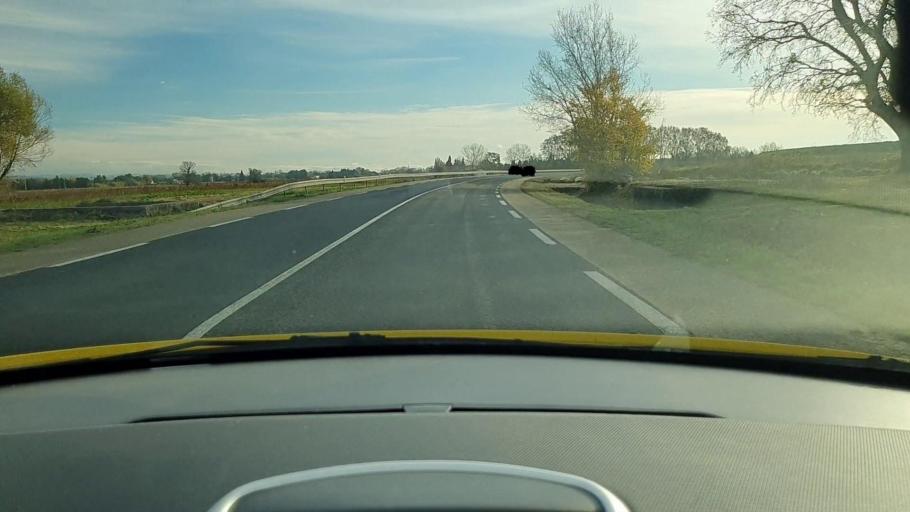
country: FR
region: Languedoc-Roussillon
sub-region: Departement du Gard
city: Fourques
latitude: 43.6991
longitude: 4.5817
